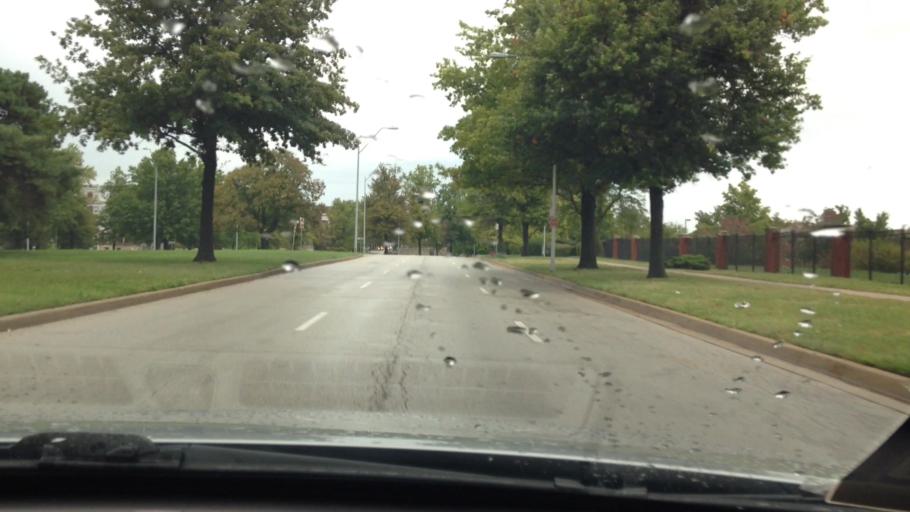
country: US
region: Missouri
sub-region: Jackson County
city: Kansas City
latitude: 39.0971
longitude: -94.5639
